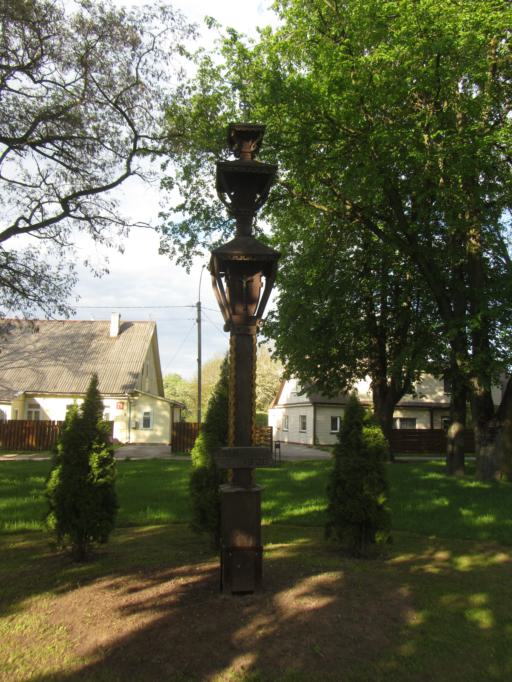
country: LT
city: Sirvintos
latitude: 55.0473
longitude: 24.9496
